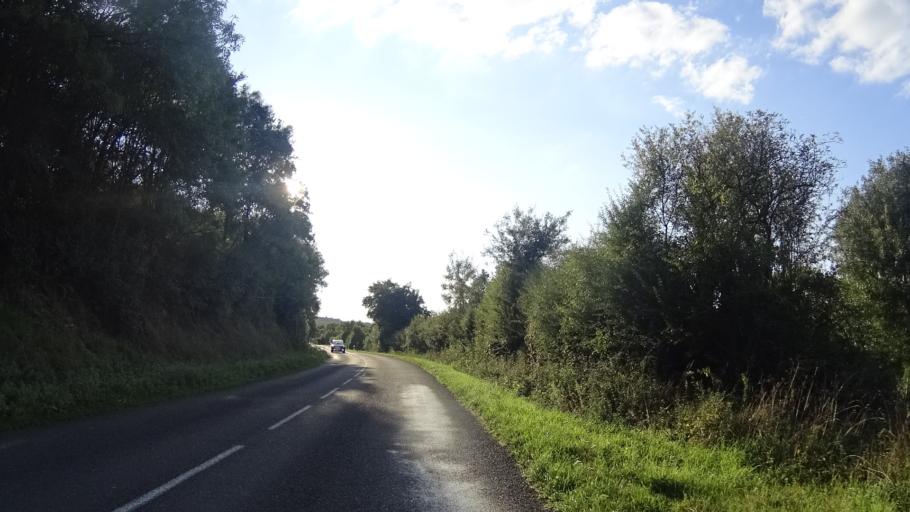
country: FR
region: Pays de la Loire
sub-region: Departement de Maine-et-Loire
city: Drain
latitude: 47.3400
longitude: -1.2324
